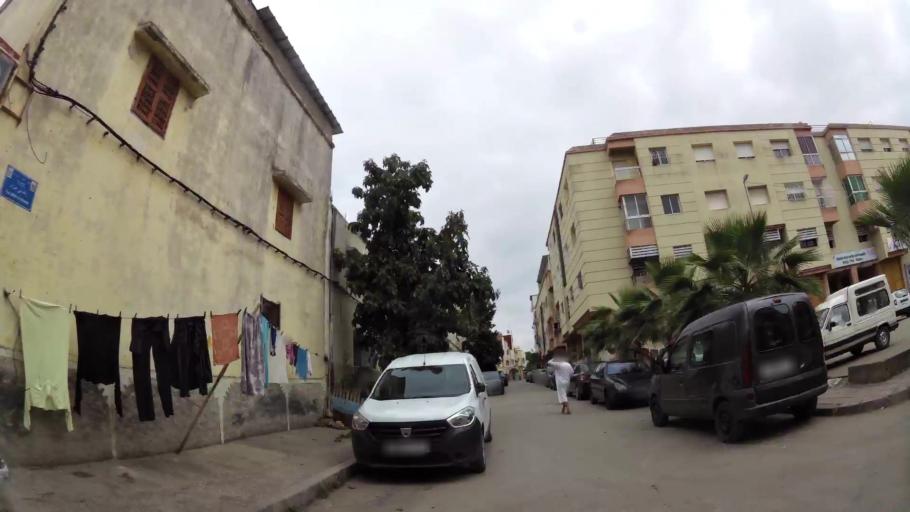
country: MA
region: Rabat-Sale-Zemmour-Zaer
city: Sale
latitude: 34.0317
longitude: -6.7992
